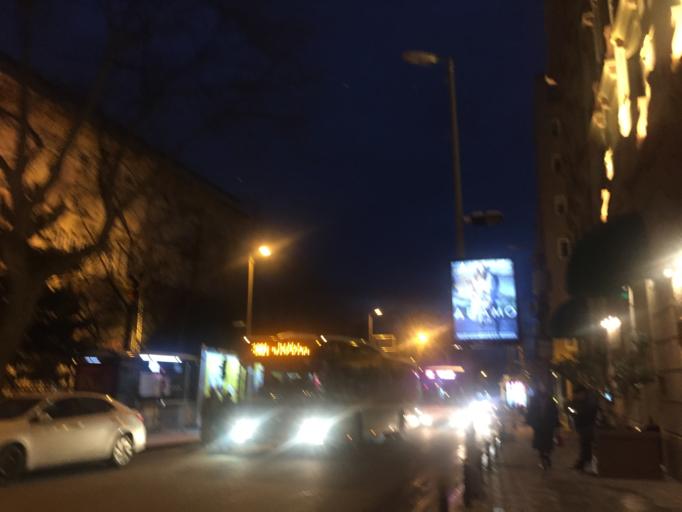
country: TR
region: Istanbul
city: Sisli
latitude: 41.0475
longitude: 28.9946
